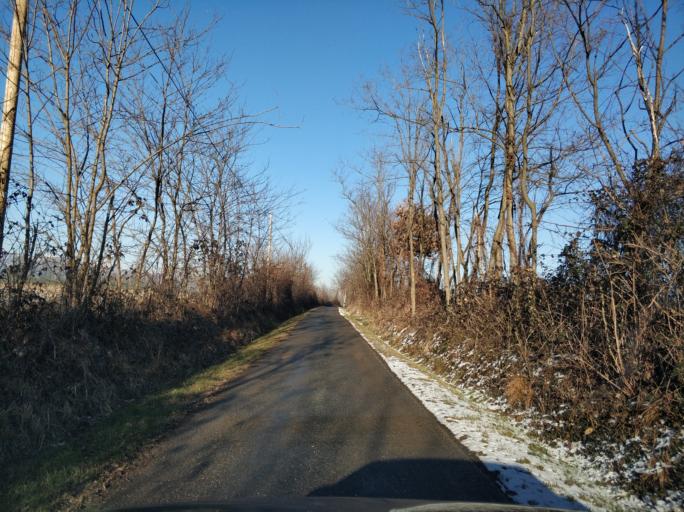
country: IT
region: Piedmont
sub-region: Provincia di Torino
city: San Francesco al Campo
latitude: 45.2273
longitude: 7.6742
